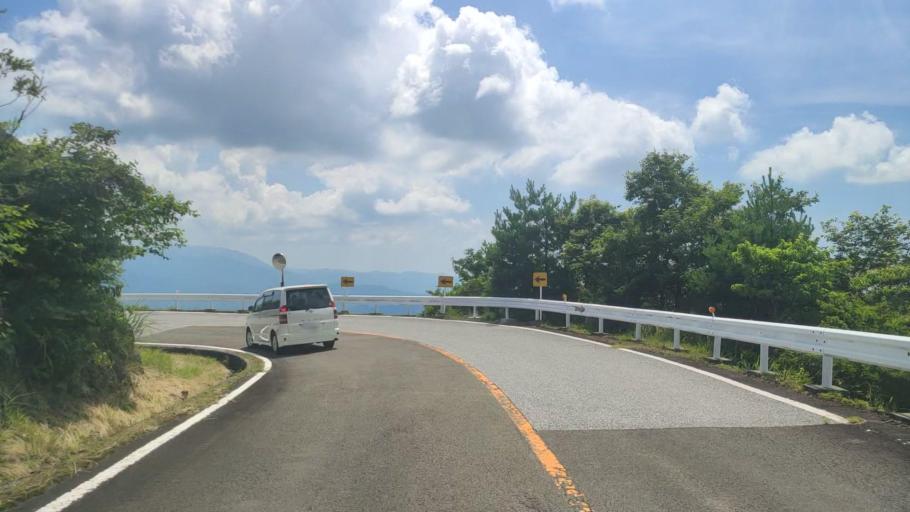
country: JP
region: Gifu
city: Tarui
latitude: 35.3993
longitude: 136.4271
